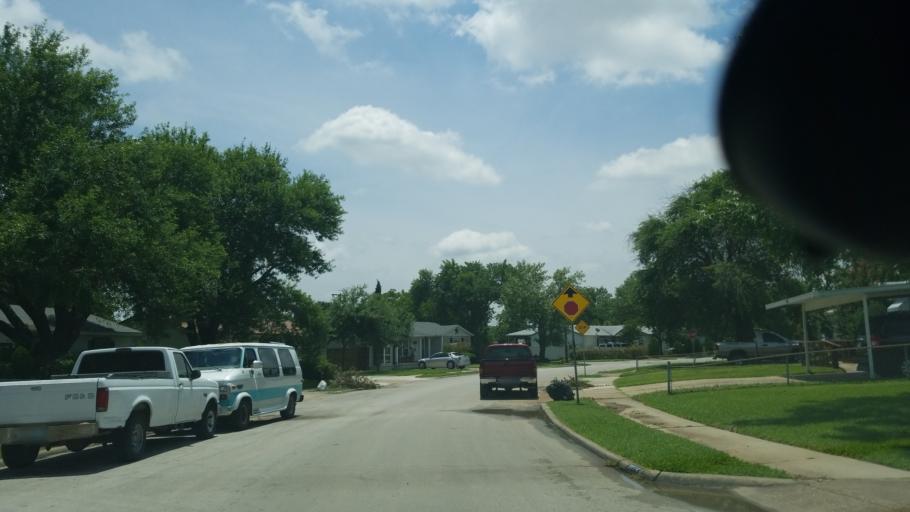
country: US
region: Texas
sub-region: Dallas County
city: Irving
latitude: 32.8455
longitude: -96.9721
